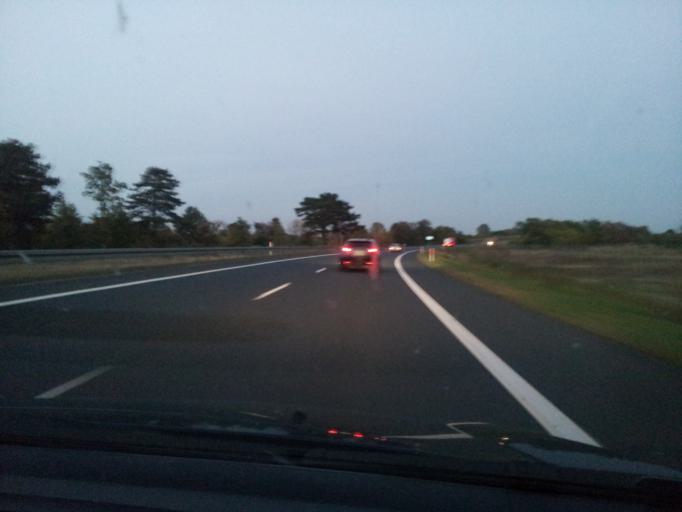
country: PL
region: Kujawsko-Pomorskie
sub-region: Torun
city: Torun
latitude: 52.9842
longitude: 18.5815
